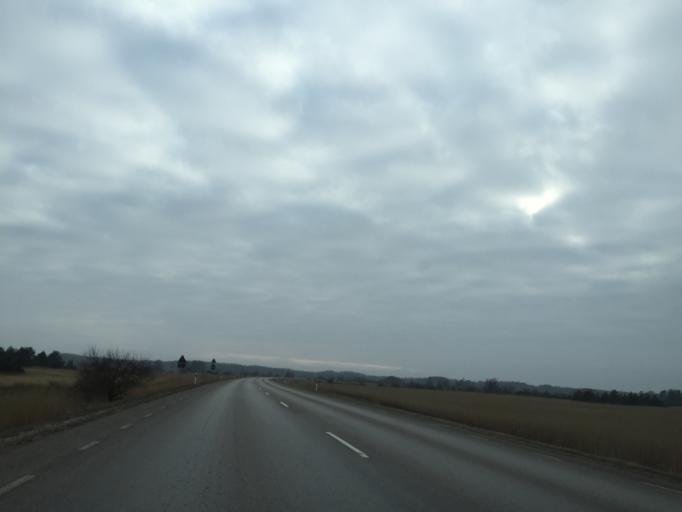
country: EE
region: Saare
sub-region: Orissaare vald
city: Orissaare
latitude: 58.5422
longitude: 23.1259
